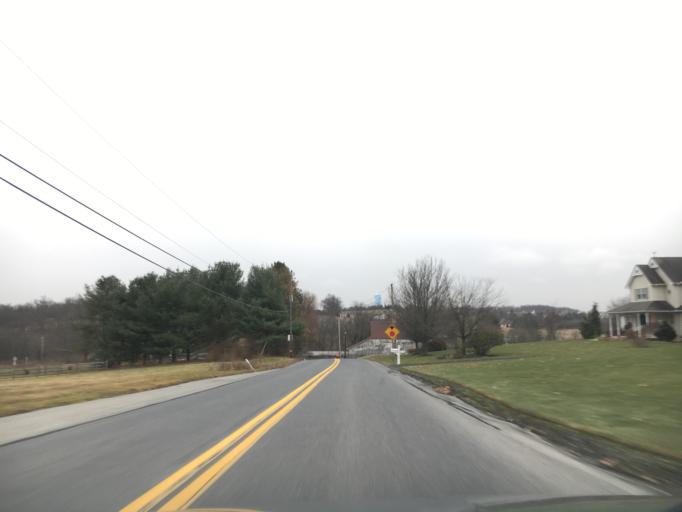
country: US
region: Pennsylvania
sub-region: Lehigh County
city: Schnecksville
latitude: 40.6998
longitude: -75.5836
